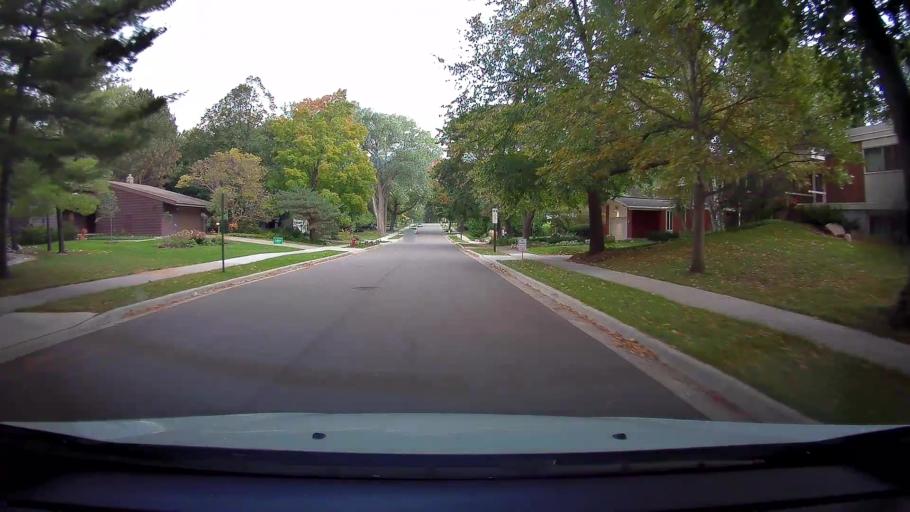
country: US
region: Minnesota
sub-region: Ramsey County
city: Lauderdale
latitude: 44.9892
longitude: -93.1914
